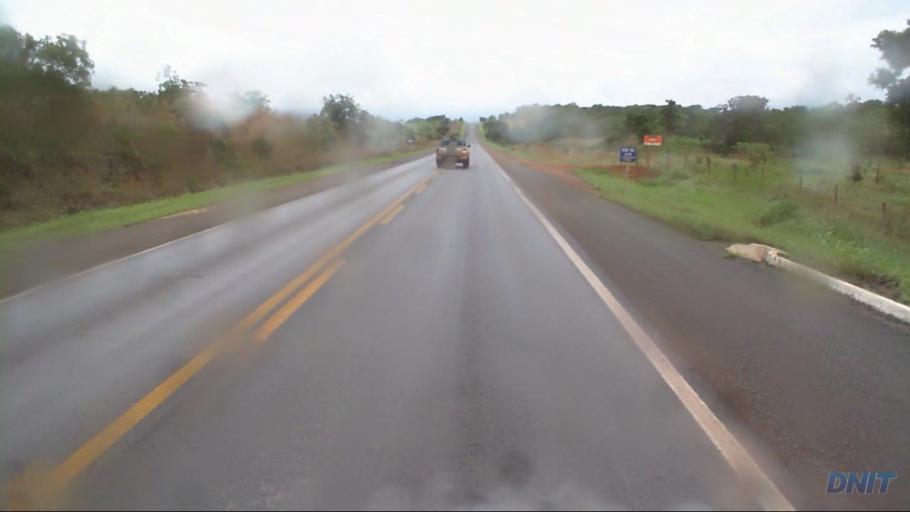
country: BR
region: Goias
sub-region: Padre Bernardo
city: Padre Bernardo
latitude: -15.1984
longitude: -48.4482
